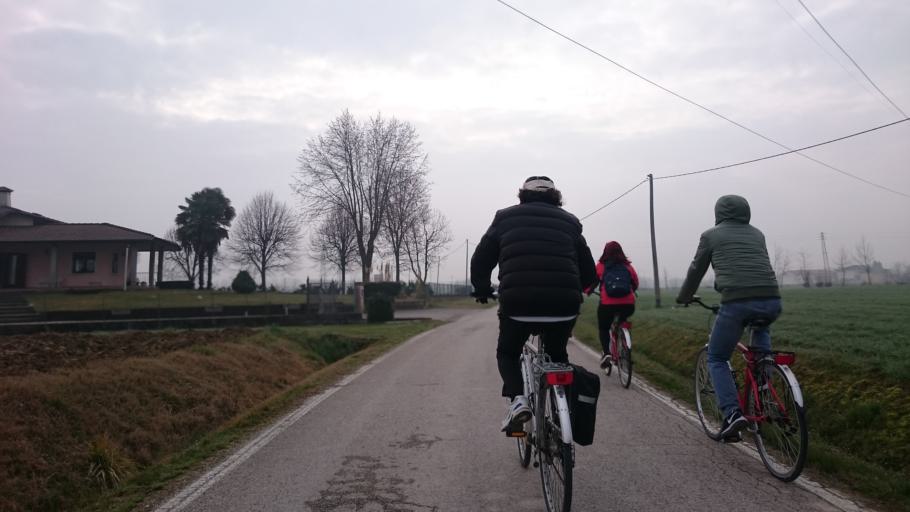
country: IT
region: Veneto
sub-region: Provincia di Vicenza
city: Longare
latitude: 45.4774
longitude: 11.6470
